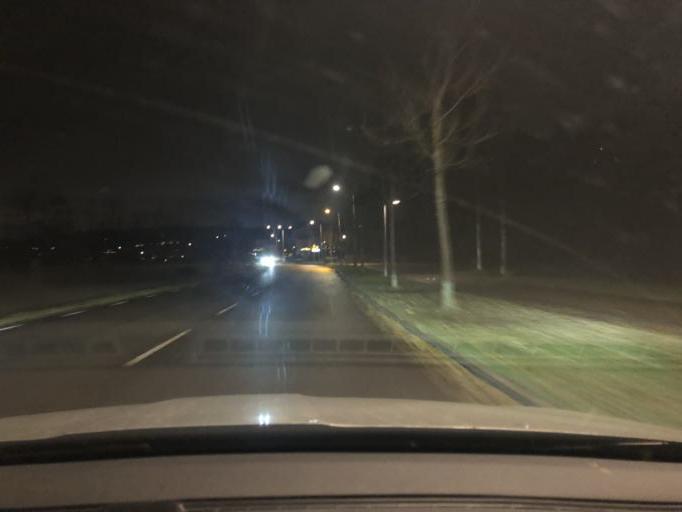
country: SE
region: Stockholm
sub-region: Huddinge Kommun
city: Huddinge
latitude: 59.2335
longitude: 17.9479
